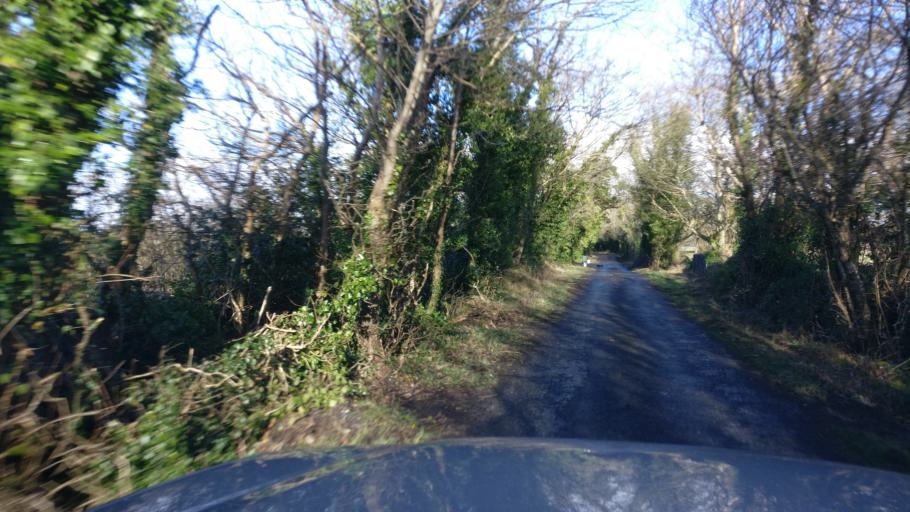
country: IE
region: Connaught
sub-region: County Galway
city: Loughrea
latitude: 53.2212
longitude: -8.6688
